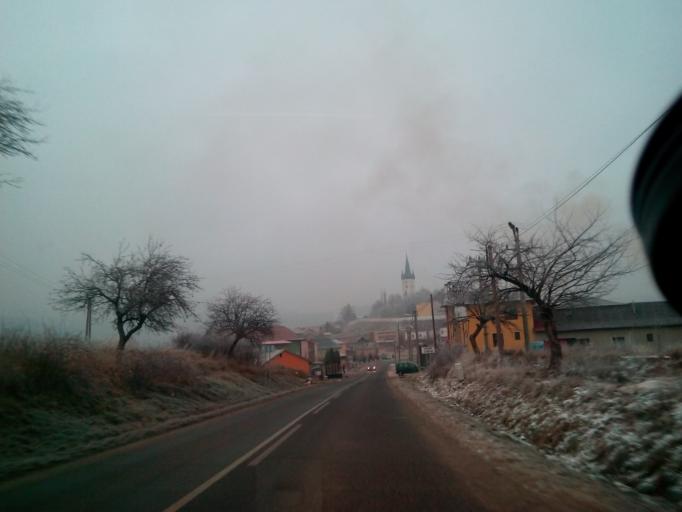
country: SK
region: Presovsky
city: Lubica
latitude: 48.9993
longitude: 20.4565
